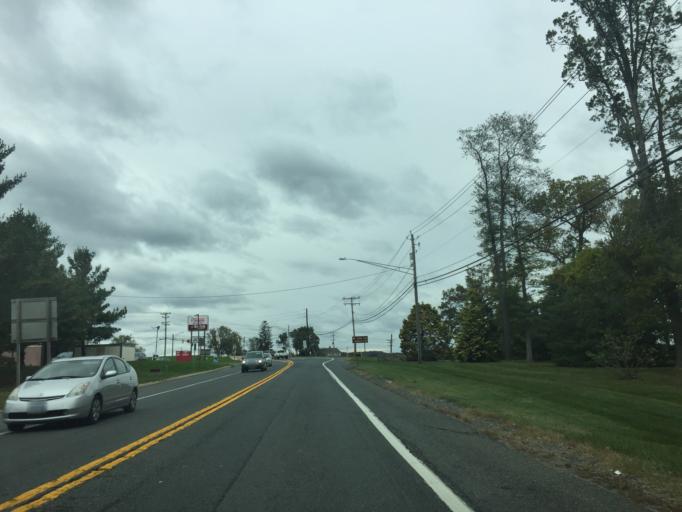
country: US
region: Maryland
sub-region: Harford County
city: Riverside
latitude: 39.5060
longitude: -76.2687
